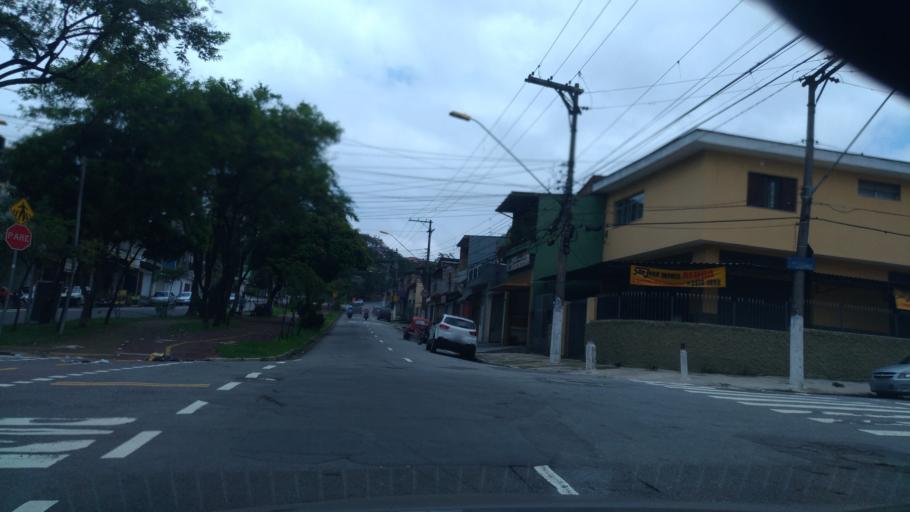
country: BR
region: Sao Paulo
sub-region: Santo Andre
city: Santo Andre
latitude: -23.6971
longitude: -46.5147
